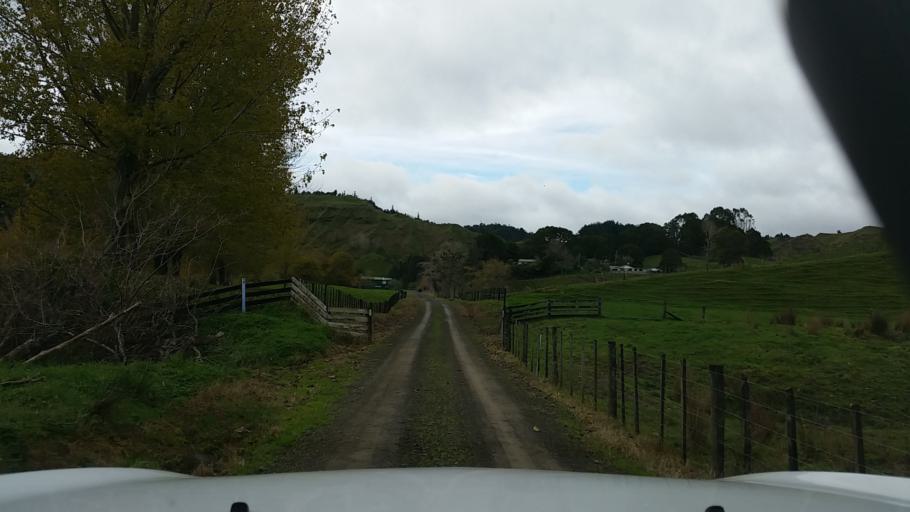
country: NZ
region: Taranaki
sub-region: New Plymouth District
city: Waitara
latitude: -38.7566
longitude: 174.7039
